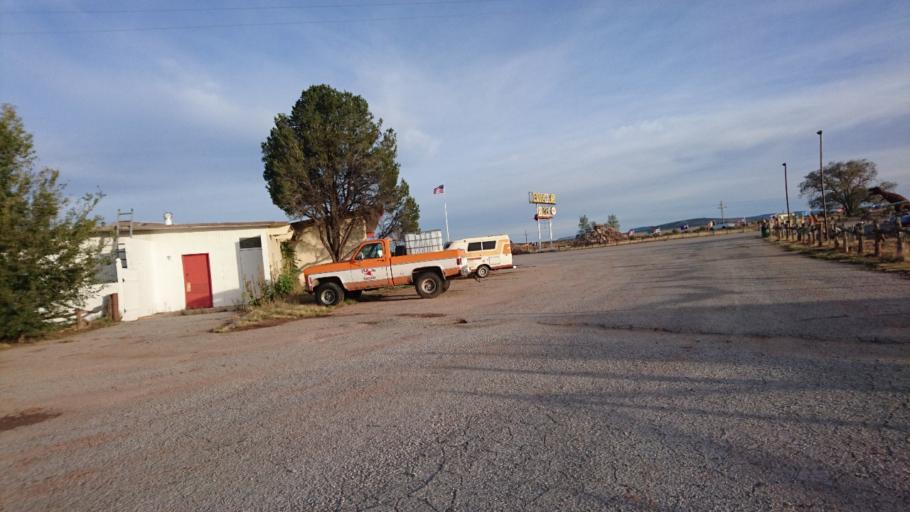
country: US
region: Arizona
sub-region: Mohave County
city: Peach Springs
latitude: 35.5284
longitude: -113.2307
